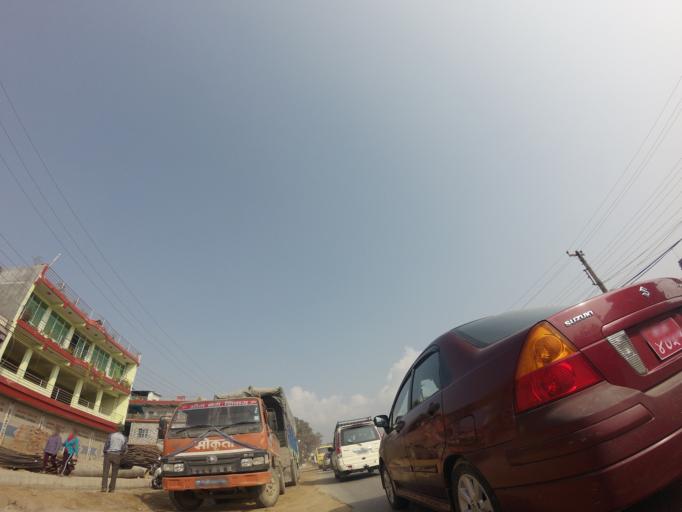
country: NP
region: Western Region
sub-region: Gandaki Zone
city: Pokhara
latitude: 28.2219
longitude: 83.9783
